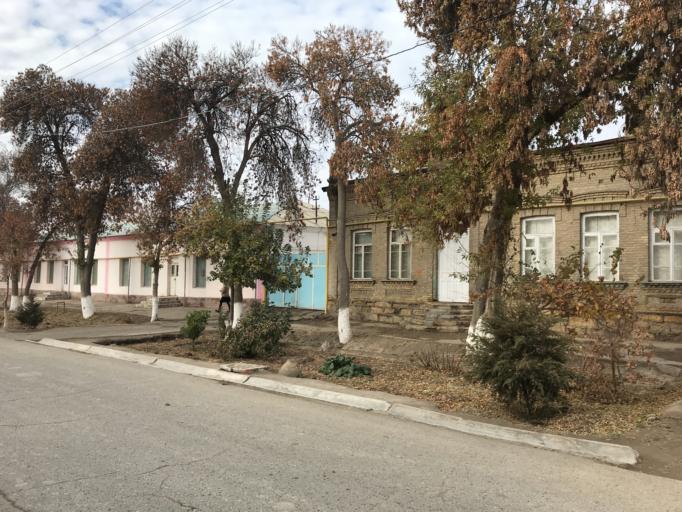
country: UZ
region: Bukhara
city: Kogon
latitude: 39.7241
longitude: 64.5545
